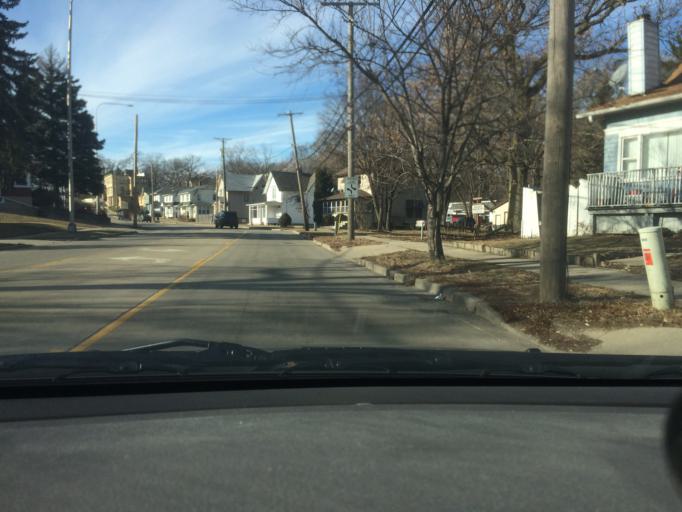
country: US
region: Illinois
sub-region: Kane County
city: Elgin
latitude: 42.0370
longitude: -88.2646
